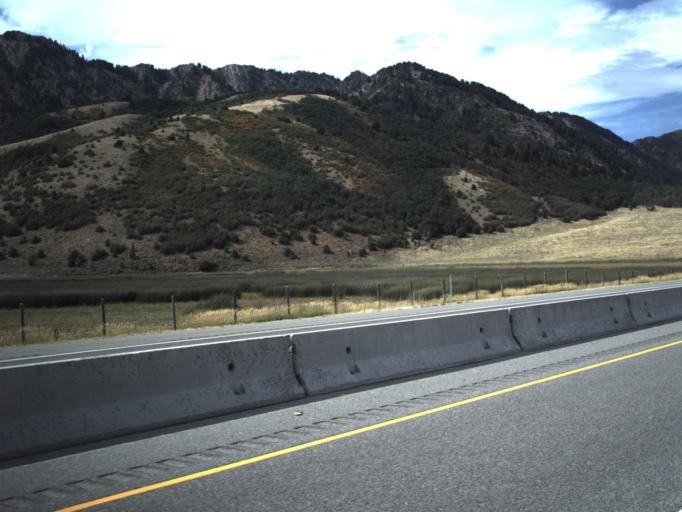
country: US
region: Utah
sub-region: Box Elder County
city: Brigham City
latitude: 41.5666
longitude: -111.9656
